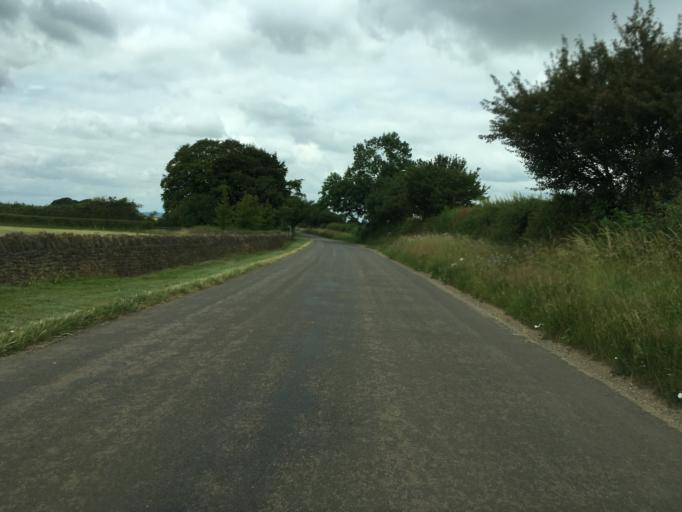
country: GB
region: England
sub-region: Oxfordshire
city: Chipping Norton
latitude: 51.9255
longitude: -1.5592
